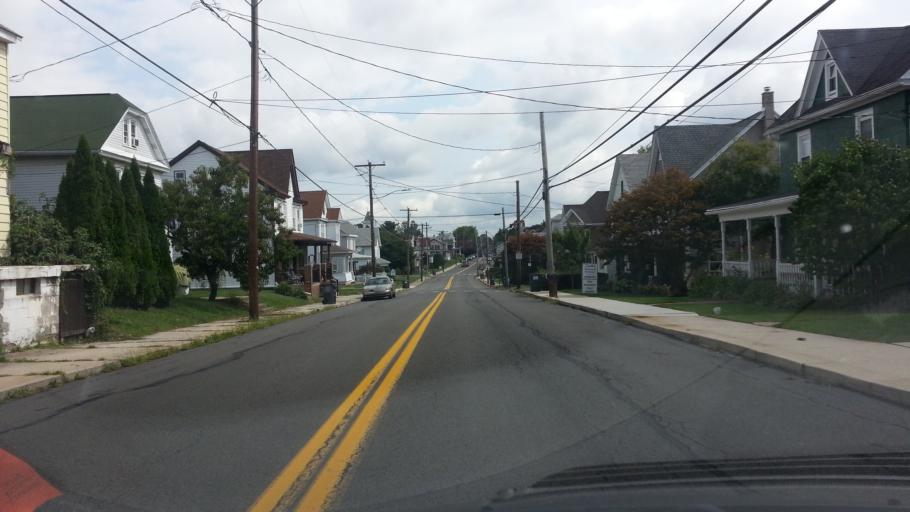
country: US
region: Pennsylvania
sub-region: Schuylkill County
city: Shenandoah Heights
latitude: 40.8574
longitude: -76.2371
